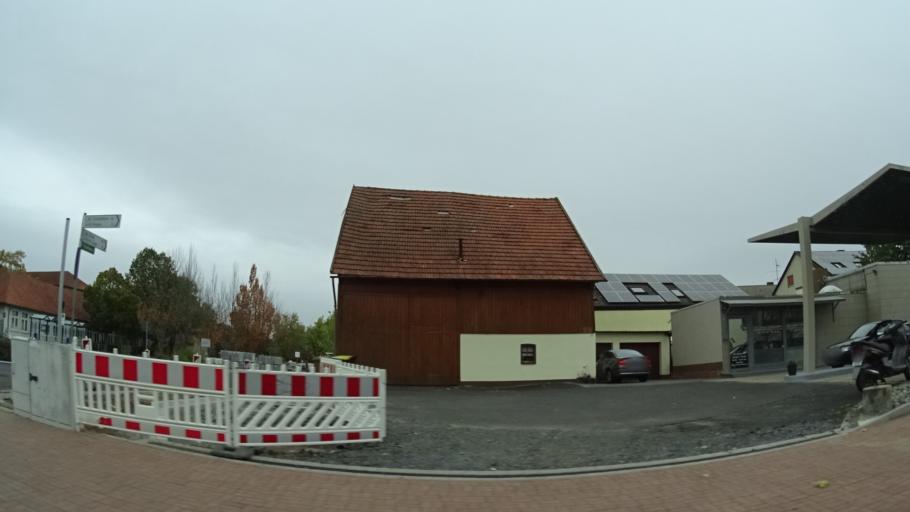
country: DE
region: Hesse
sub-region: Regierungsbezirk Kassel
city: Neuhof
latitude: 50.4528
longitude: 9.6164
